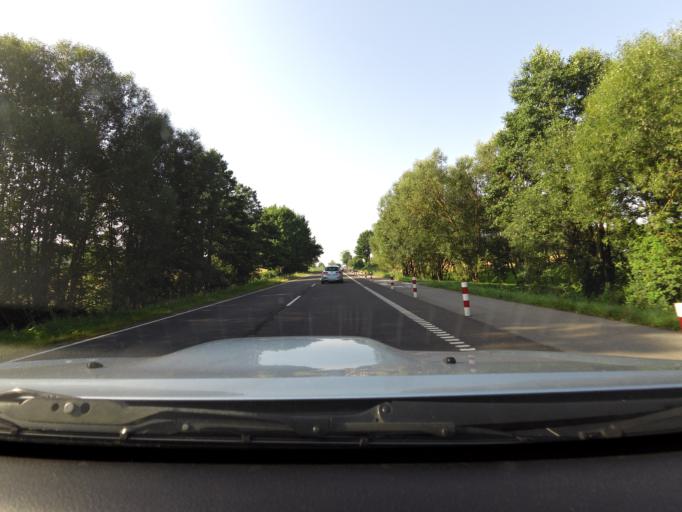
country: LT
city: Lazdijai
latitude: 54.1486
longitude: 23.4691
